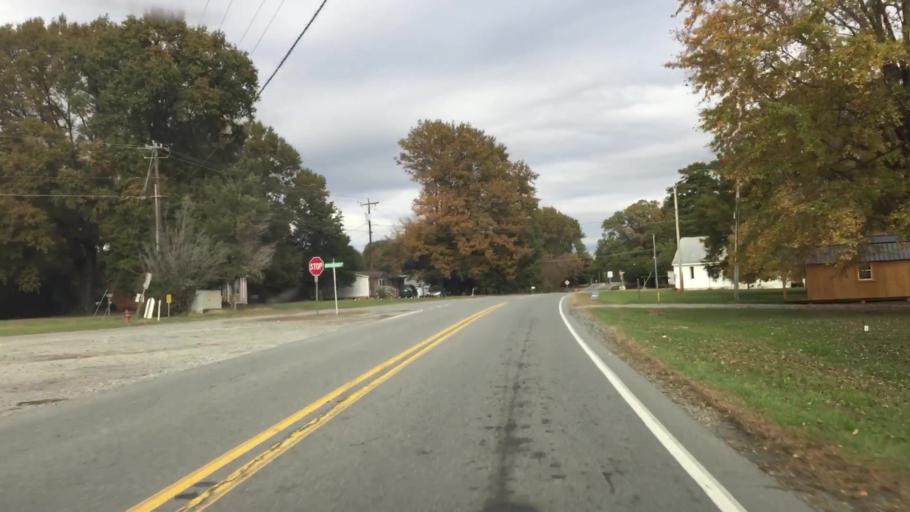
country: US
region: North Carolina
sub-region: Rockingham County
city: Reidsville
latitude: 36.3297
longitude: -79.7088
